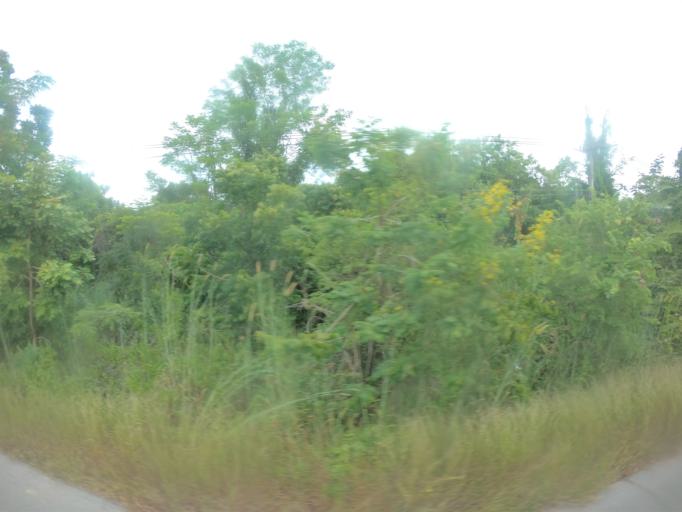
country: TH
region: Maha Sarakham
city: Kantharawichai
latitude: 16.3377
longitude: 103.2207
